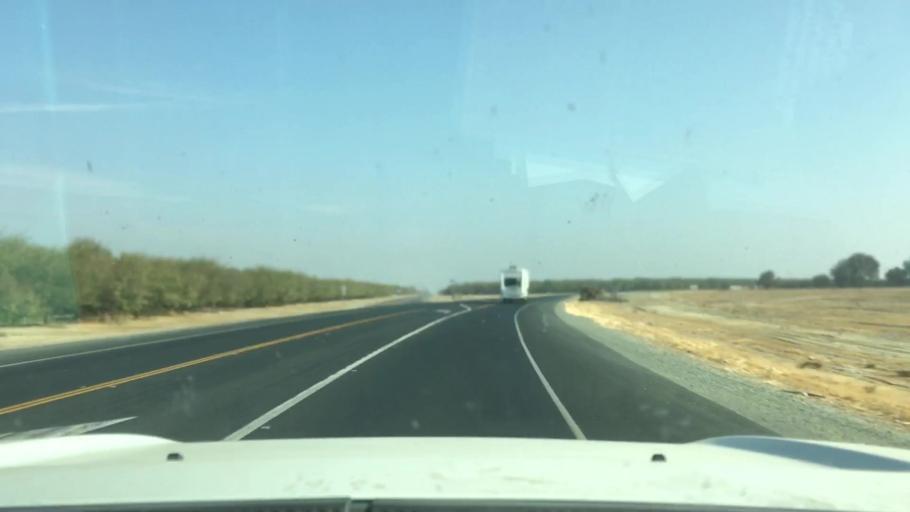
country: US
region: California
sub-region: Kern County
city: Lost Hills
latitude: 35.6158
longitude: -119.5939
